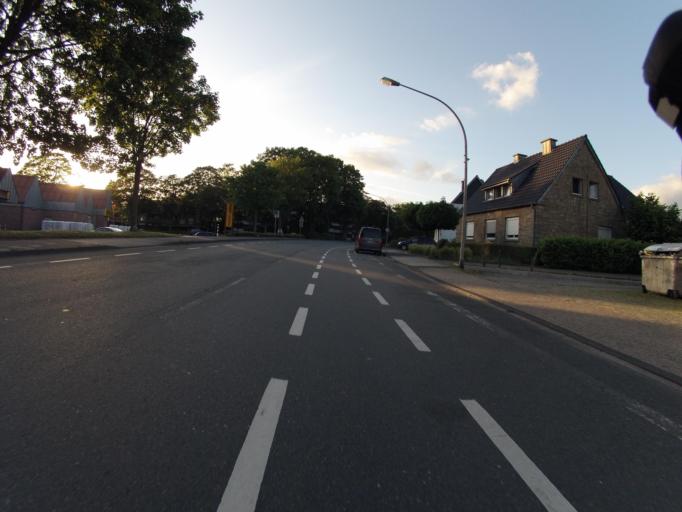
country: DE
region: North Rhine-Westphalia
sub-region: Regierungsbezirk Munster
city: Mettingen
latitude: 52.2684
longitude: 7.7880
